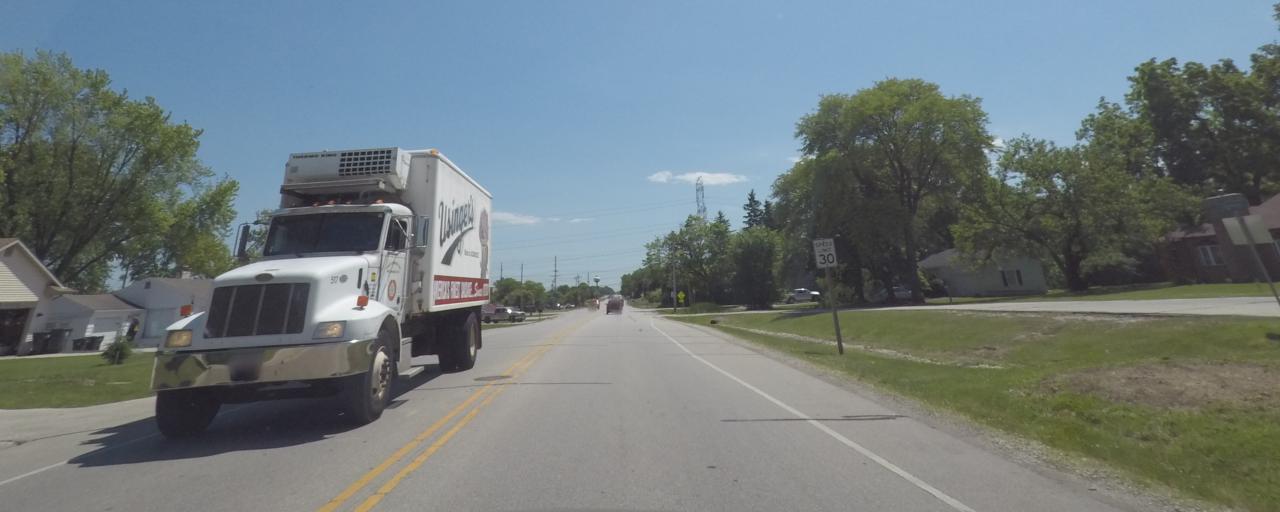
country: US
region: Wisconsin
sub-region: Waukesha County
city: New Berlin
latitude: 43.0122
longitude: -88.1271
